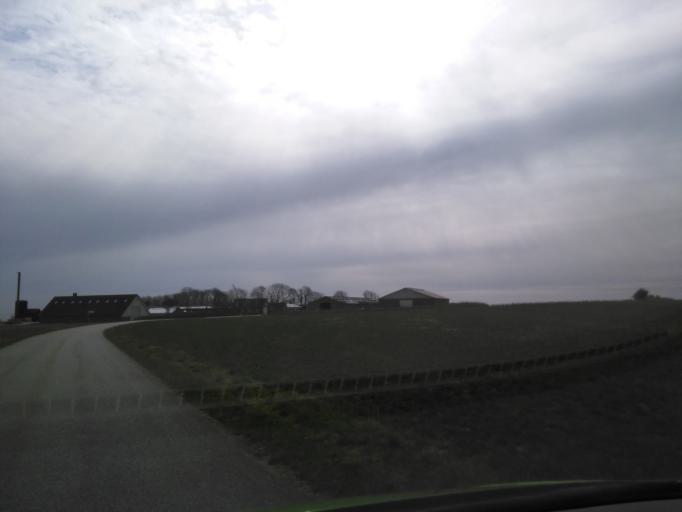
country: DK
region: Central Jutland
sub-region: Odder Kommune
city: Odder
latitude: 55.9509
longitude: 10.2502
